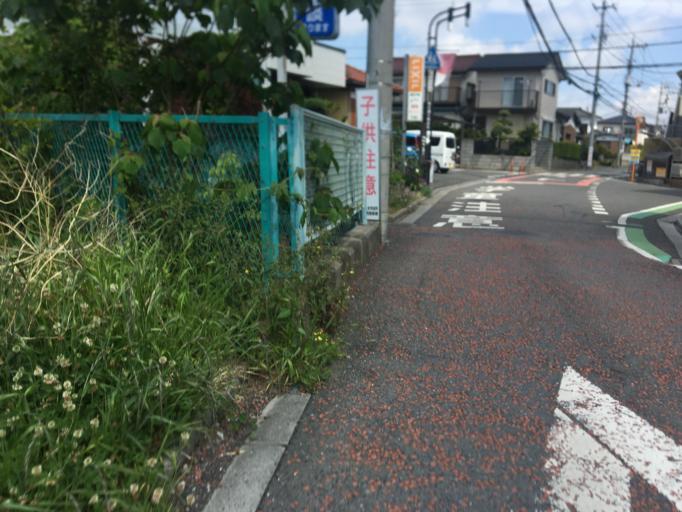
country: JP
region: Saitama
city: Yono
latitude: 35.8659
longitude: 139.6032
